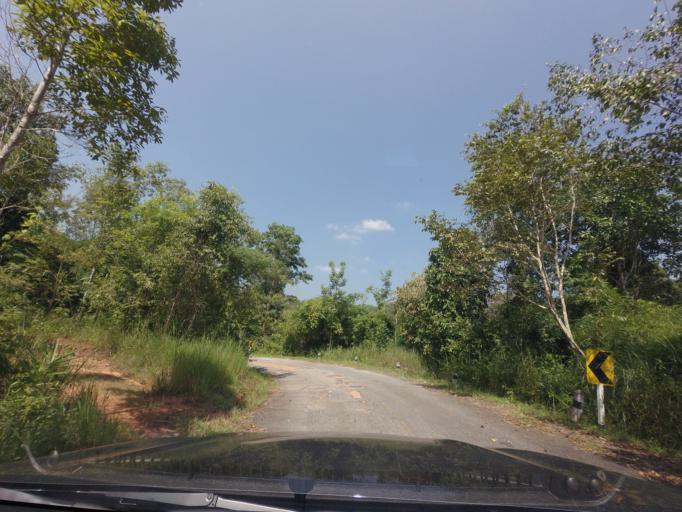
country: TH
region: Loei
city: Na Haeo
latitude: 17.5701
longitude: 100.9762
